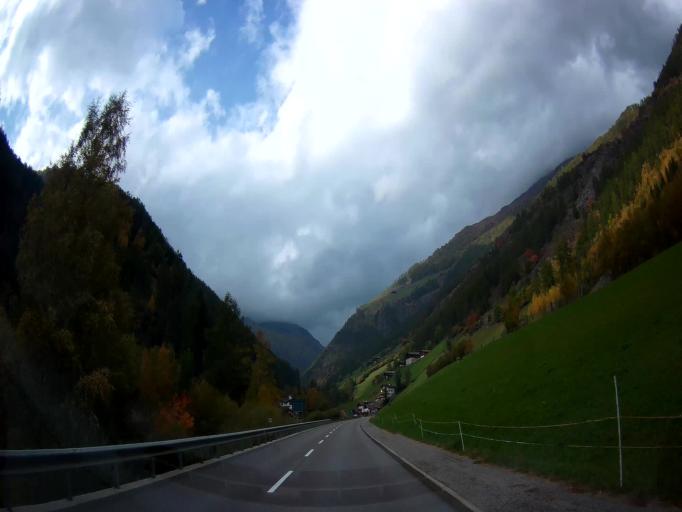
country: IT
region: Trentino-Alto Adige
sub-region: Bolzano
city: Senales
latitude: 46.7101
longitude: 10.9017
